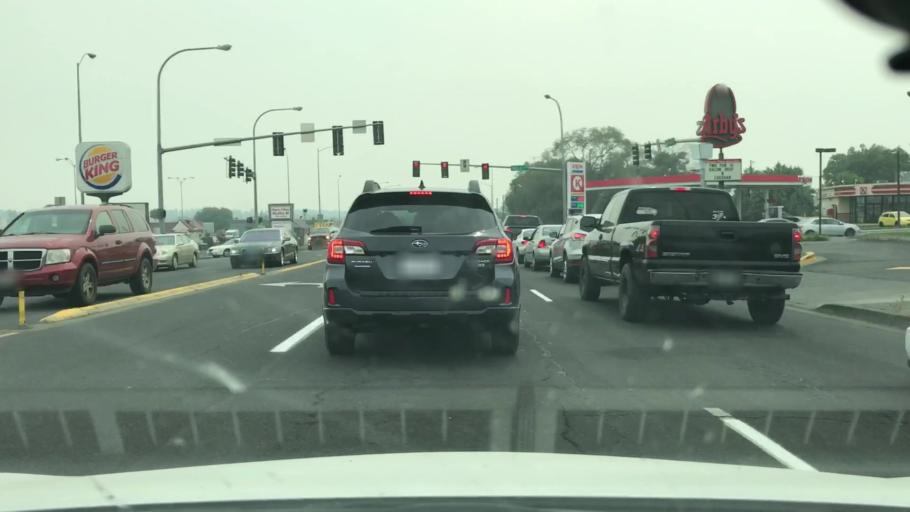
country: US
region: Washington
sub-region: Grant County
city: Moses Lake
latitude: 47.1390
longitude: -119.2784
